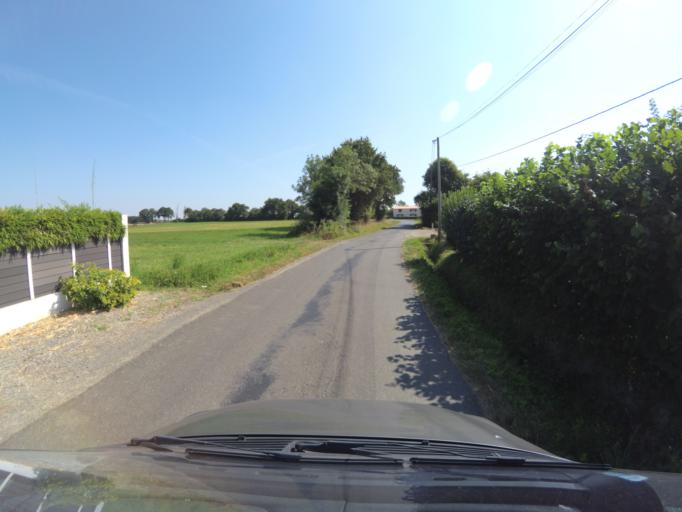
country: FR
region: Pays de la Loire
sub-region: Departement de la Loire-Atlantique
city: Vieillevigne
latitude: 46.9880
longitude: -1.4619
